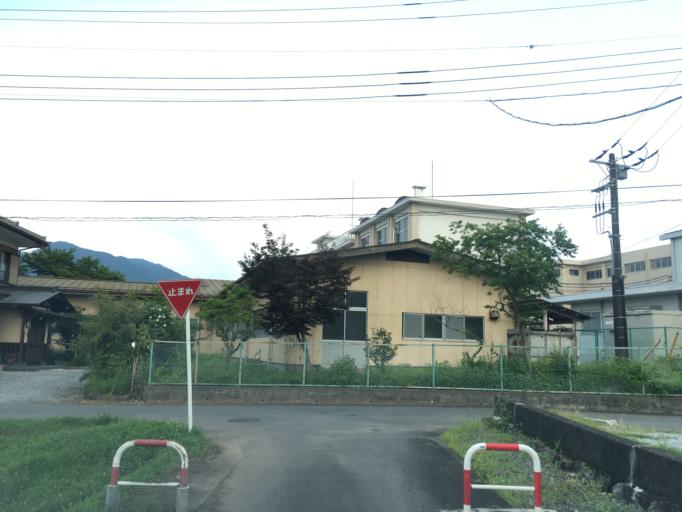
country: JP
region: Saitama
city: Chichibu
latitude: 35.9929
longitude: 139.0985
